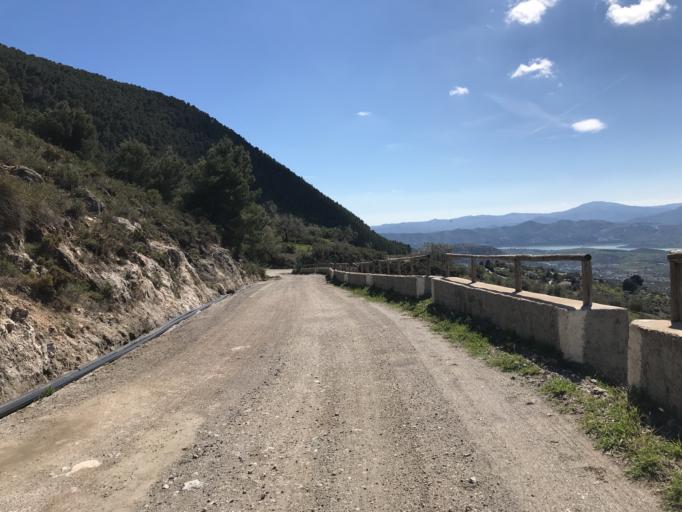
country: ES
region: Andalusia
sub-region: Provincia de Malaga
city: Alcaucin
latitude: 36.9160
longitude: -4.1021
